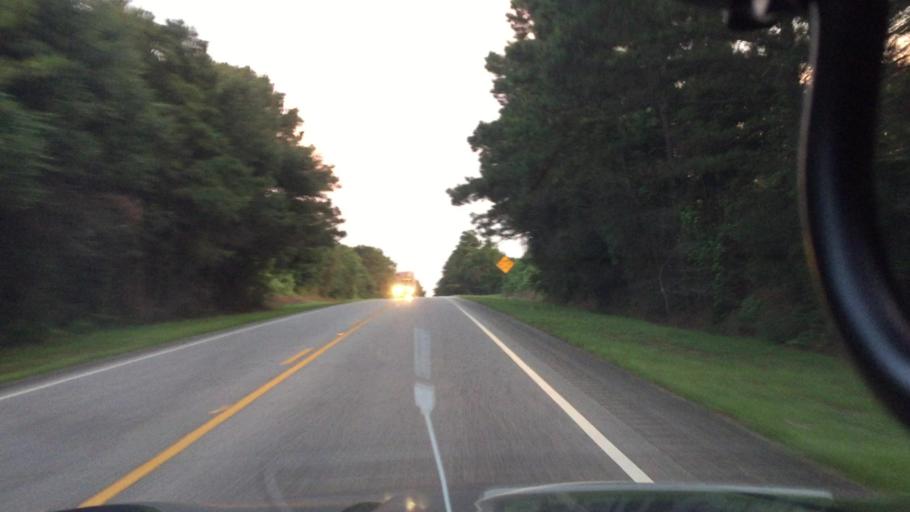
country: US
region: Alabama
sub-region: Coffee County
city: Enterprise
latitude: 31.3689
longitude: -85.8693
